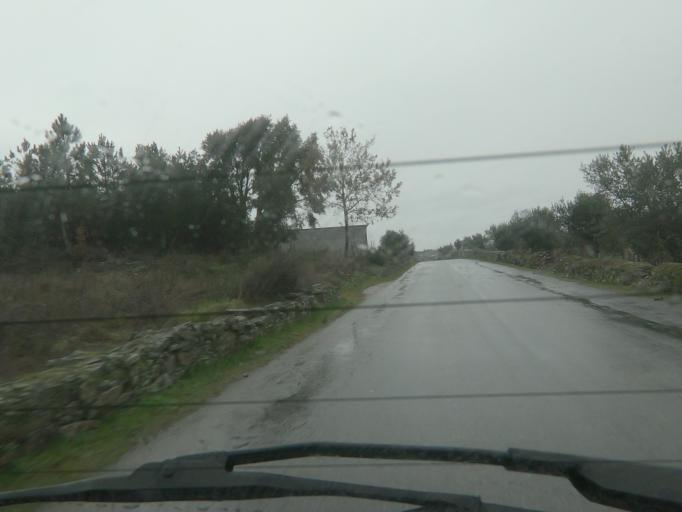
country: PT
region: Vila Real
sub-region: Peso da Regua
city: Peso da Regua
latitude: 41.1896
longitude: -7.7102
